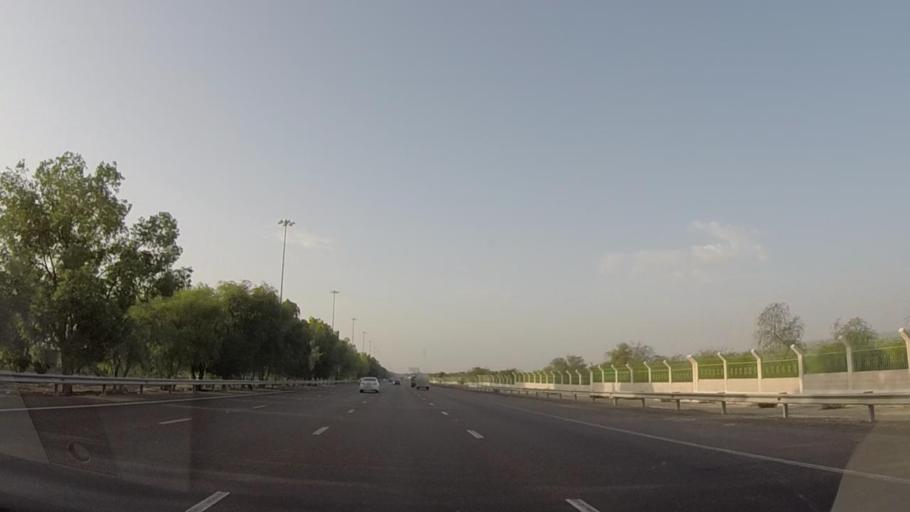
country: AE
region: Dubai
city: Dubai
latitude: 24.7896
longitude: 54.8586
